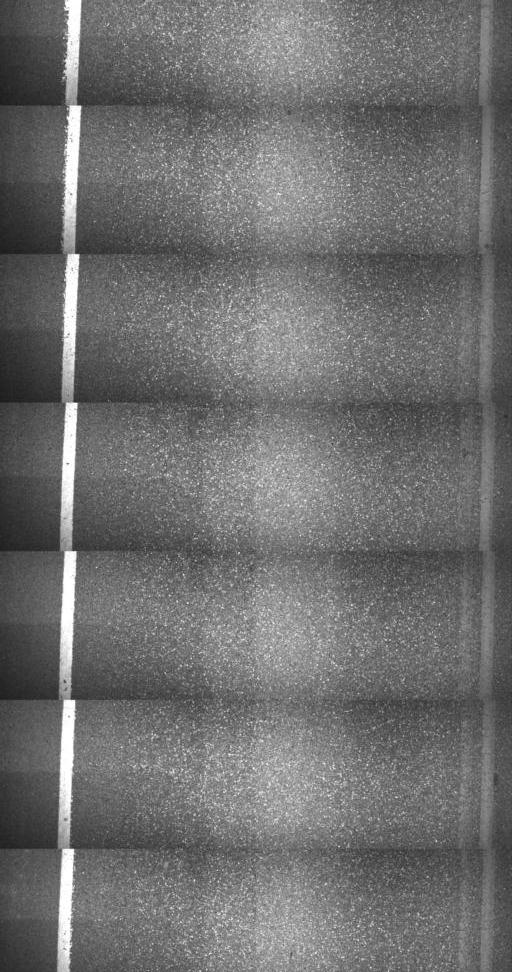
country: US
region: Vermont
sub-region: Chittenden County
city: Hinesburg
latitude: 44.3133
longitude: -73.0768
